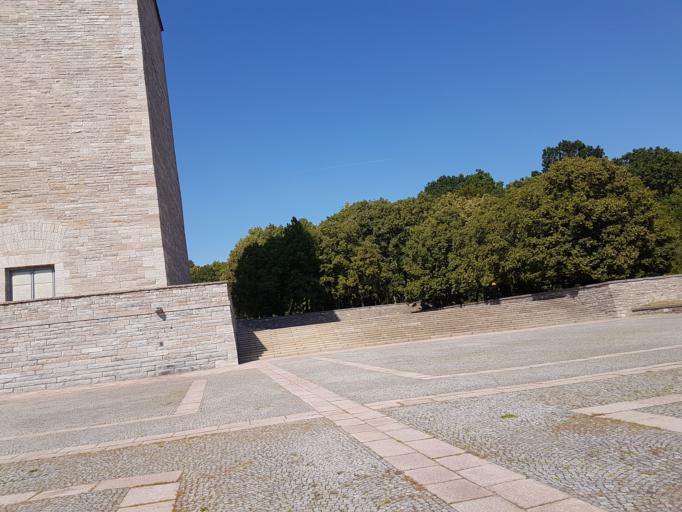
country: DE
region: Thuringia
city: Hopfgarten
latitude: 51.0105
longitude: 11.2592
